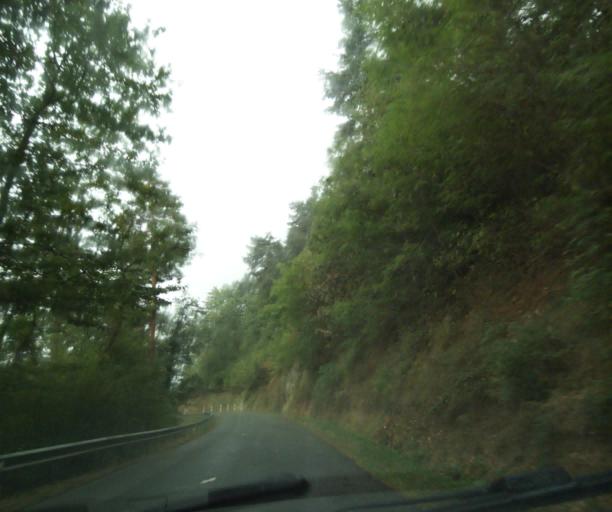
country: FR
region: Auvergne
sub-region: Departement du Puy-de-Dome
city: Ceyrat
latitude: 45.7289
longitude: 3.0605
